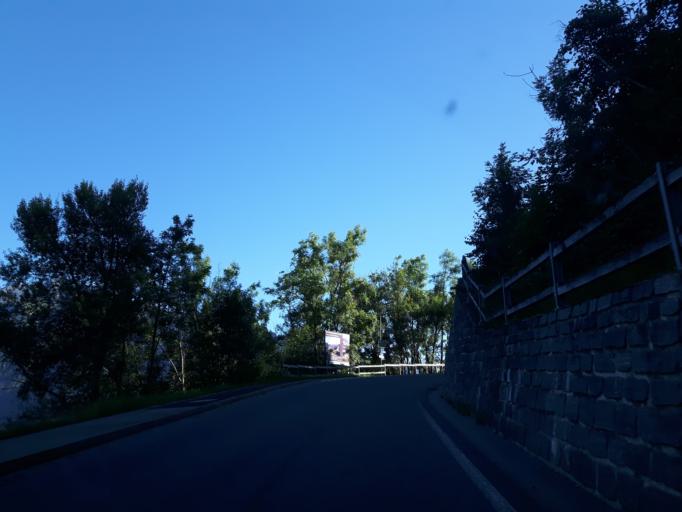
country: CH
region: Grisons
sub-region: Surselva District
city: Laax
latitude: 46.8058
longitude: 9.2489
